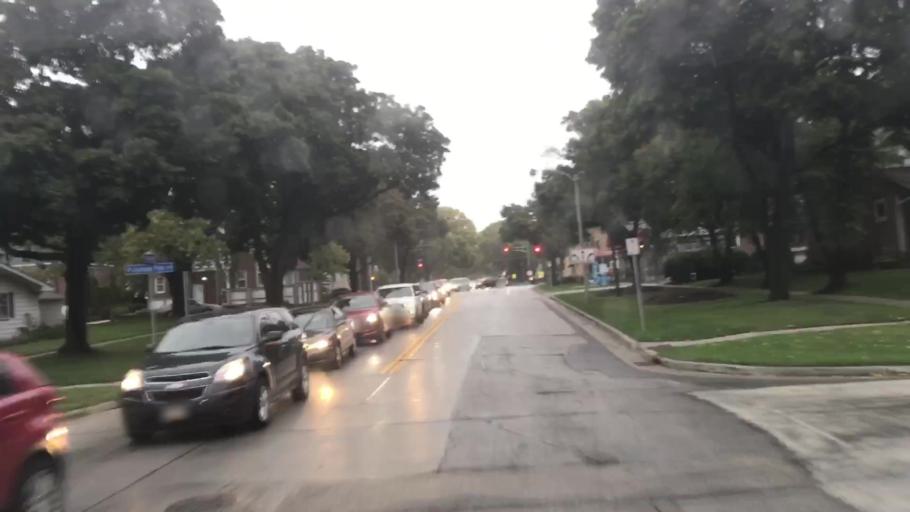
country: US
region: Wisconsin
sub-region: Milwaukee County
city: Wauwatosa
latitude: 43.0594
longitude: -88.0274
